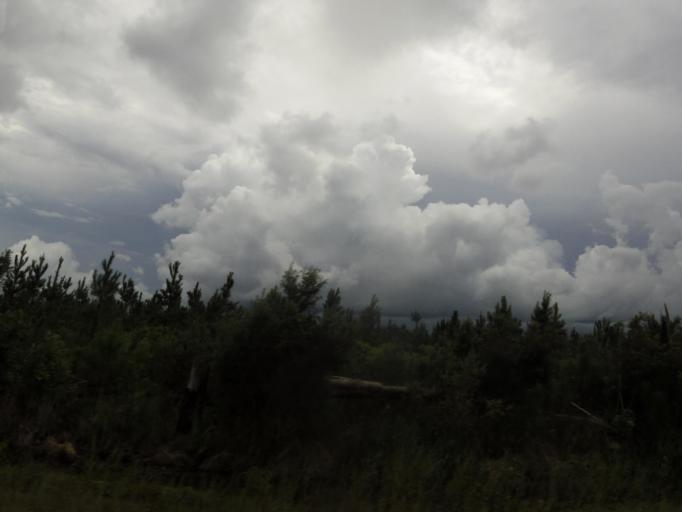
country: US
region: Florida
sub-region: Baker County
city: Macclenny
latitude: 30.5173
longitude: -82.1047
